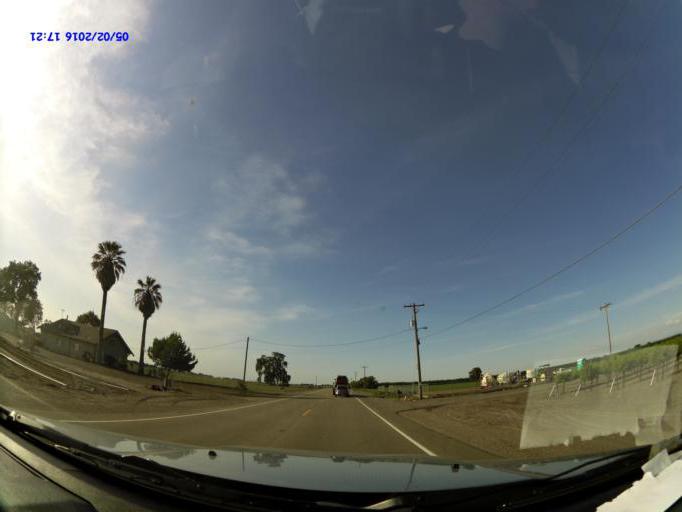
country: US
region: California
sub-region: San Joaquin County
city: Manteca
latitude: 37.8514
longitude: -121.1454
